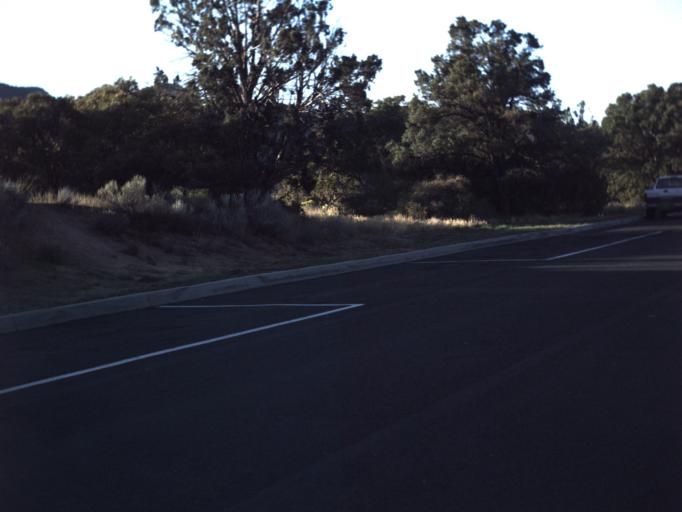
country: US
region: Utah
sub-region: Iron County
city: Cedar City
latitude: 37.5168
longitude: -113.2120
